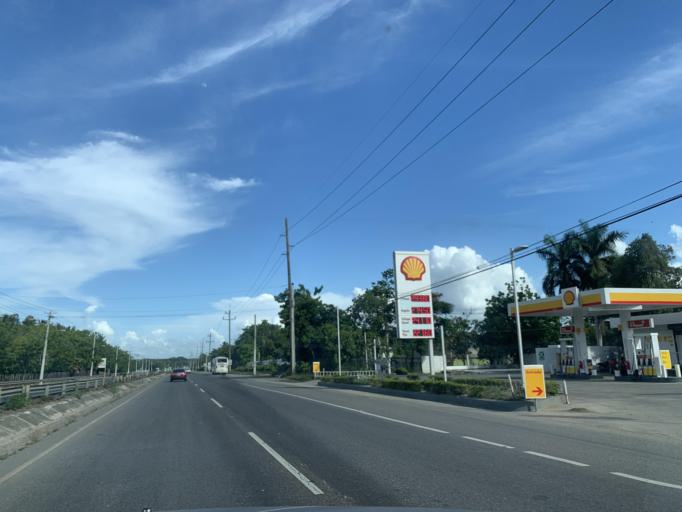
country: DO
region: Santiago
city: Villa Gonzalez
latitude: 19.5296
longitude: -70.7765
